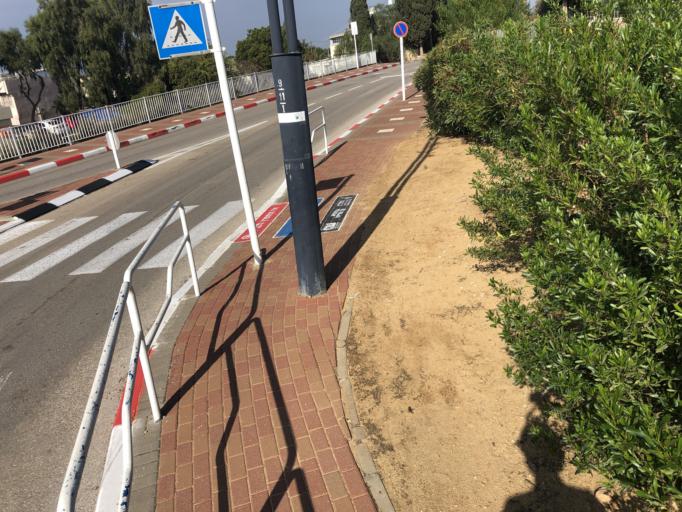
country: IL
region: Northern District
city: `Akko
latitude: 32.9365
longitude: 35.0919
